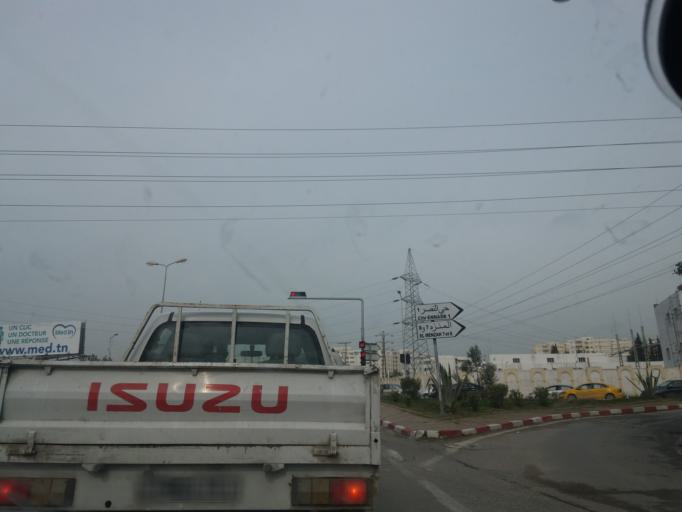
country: TN
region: Tunis
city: Tunis
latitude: 36.8503
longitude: 10.1554
